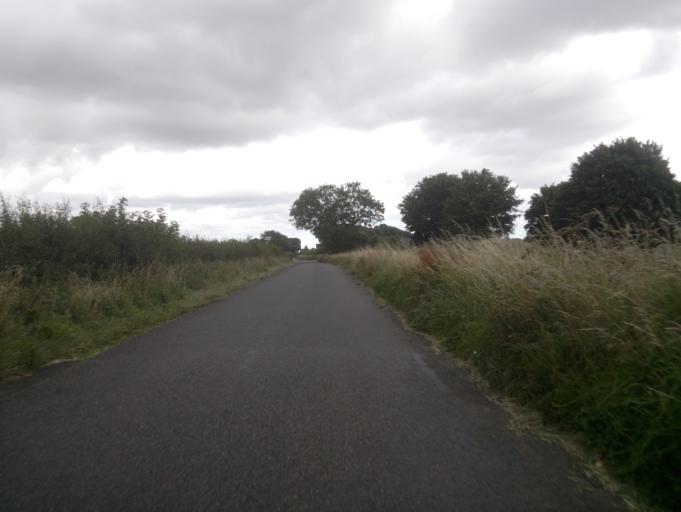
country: GB
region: England
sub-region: Gloucestershire
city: Chalford
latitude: 51.7771
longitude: -2.0993
